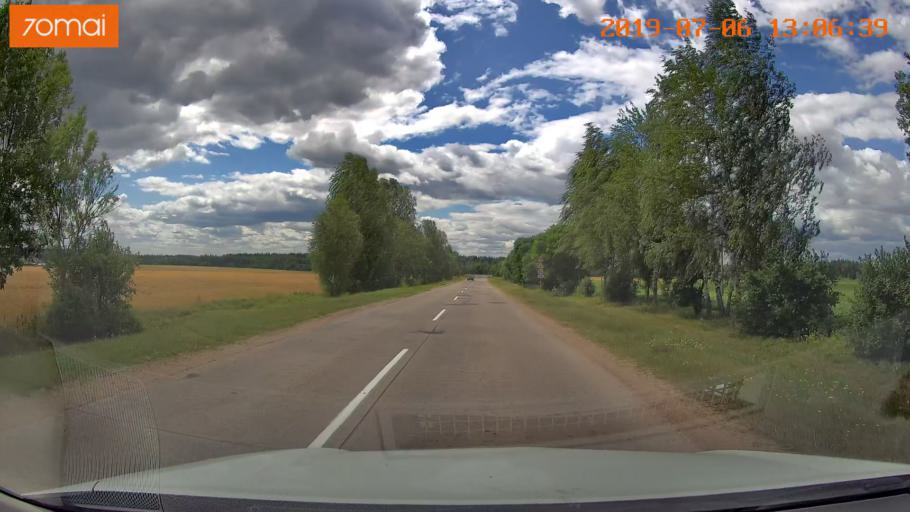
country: BY
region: Minsk
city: Dzyarzhynsk
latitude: 53.6794
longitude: 27.0503
